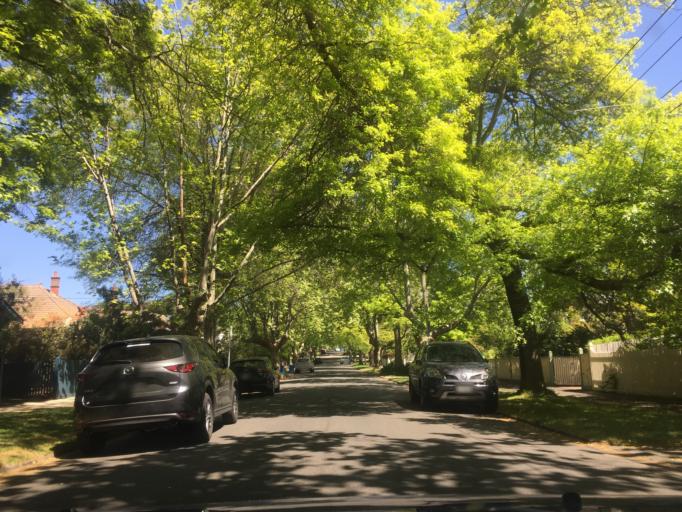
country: AU
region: Victoria
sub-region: Boroondara
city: Canterbury
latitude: -37.8259
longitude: 145.0816
